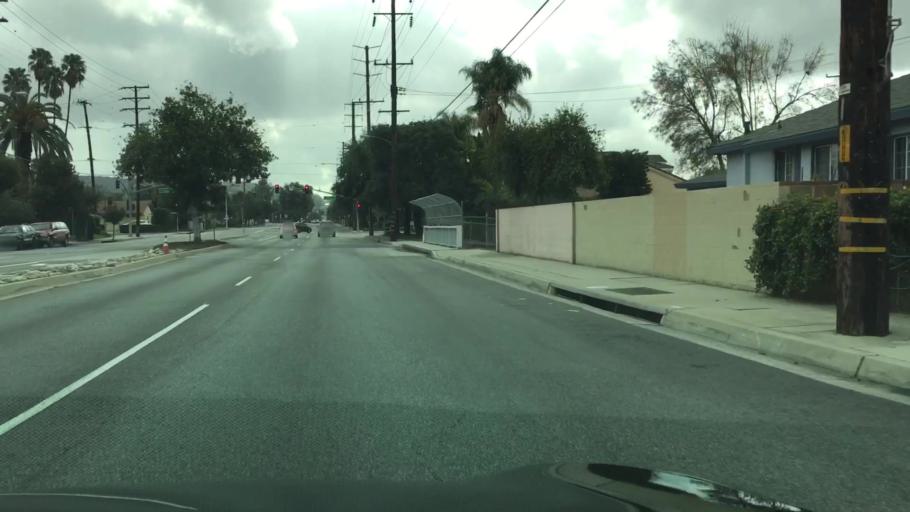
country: US
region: California
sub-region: Los Angeles County
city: Covina
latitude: 34.0658
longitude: -117.9079
